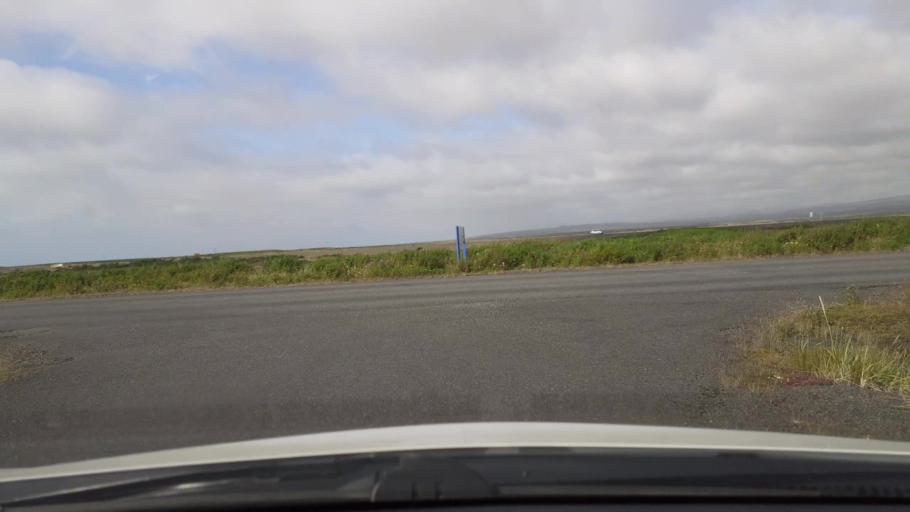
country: IS
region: South
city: THorlakshoefn
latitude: 63.8678
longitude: -21.3823
